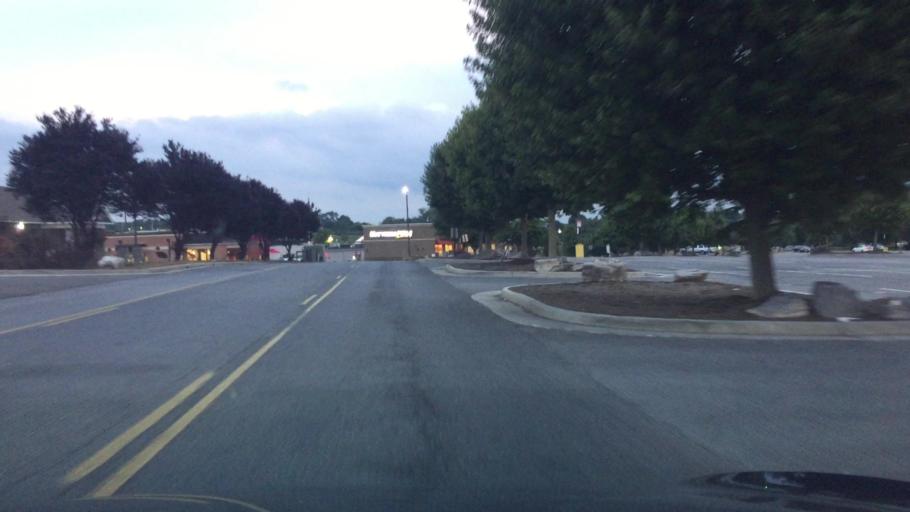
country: US
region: Virginia
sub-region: Wythe County
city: Wytheville
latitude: 36.9581
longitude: -81.0993
